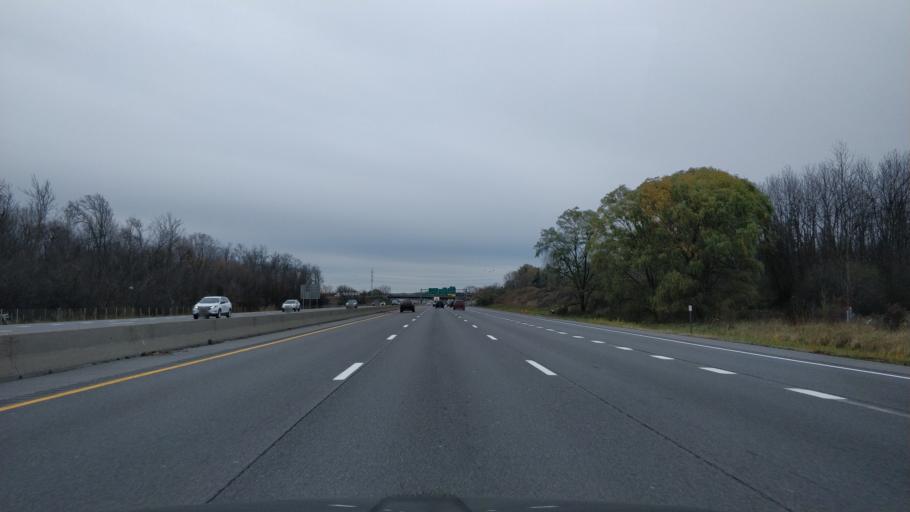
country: US
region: New York
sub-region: Onondaga County
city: Mattydale
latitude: 43.1000
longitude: -76.1570
